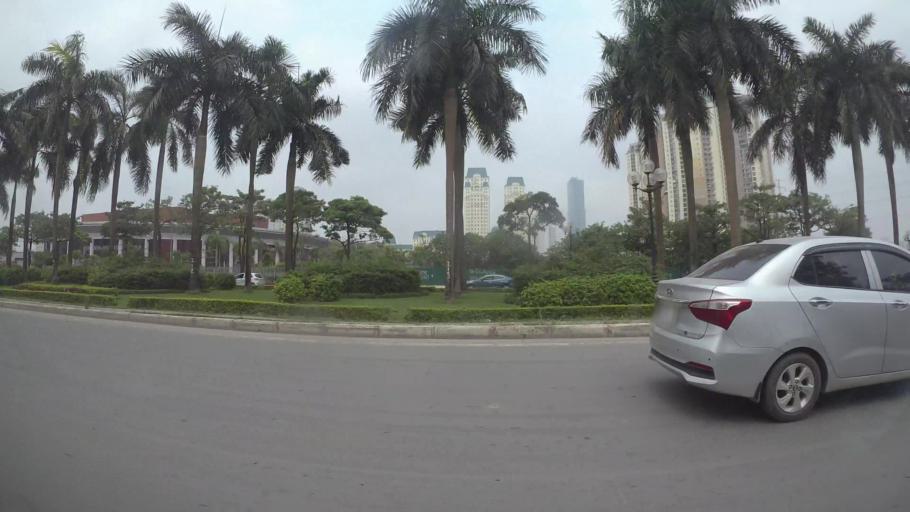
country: VN
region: Ha Noi
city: Cau Dien
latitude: 21.0111
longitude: 105.7717
